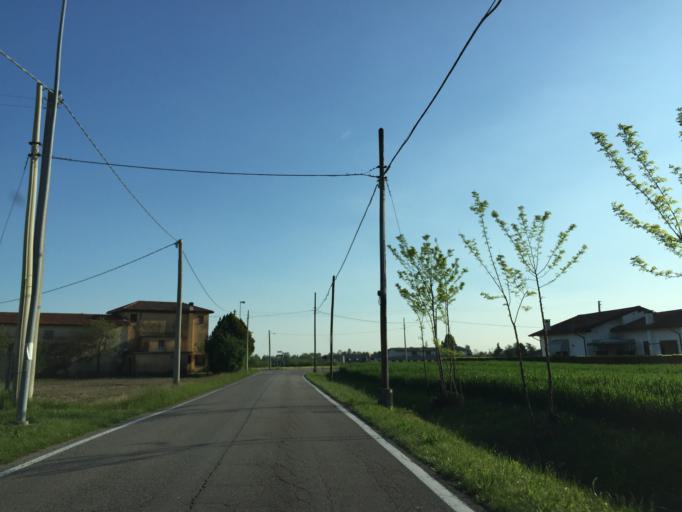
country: IT
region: Friuli Venezia Giulia
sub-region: Provincia di Pordenone
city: Tamai
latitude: 45.9615
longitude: 12.5724
